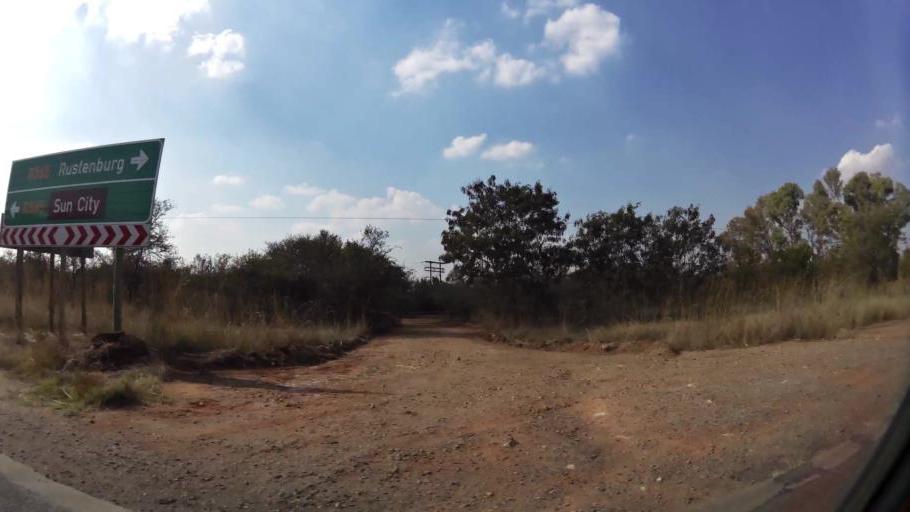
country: ZA
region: North-West
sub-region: Bojanala Platinum District Municipality
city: Rustenburg
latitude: -25.5418
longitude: 27.1241
